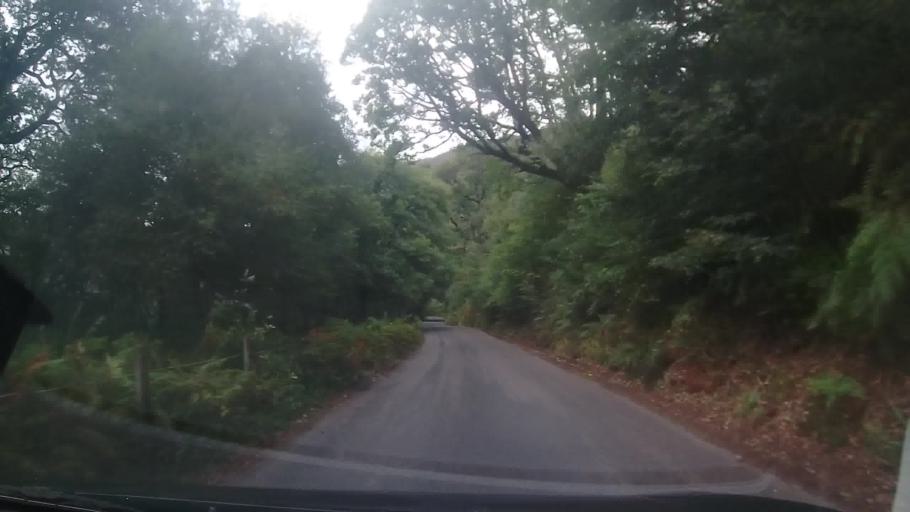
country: GB
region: Wales
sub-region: Sir Powys
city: Rhayader
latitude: 52.2695
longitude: -3.5914
